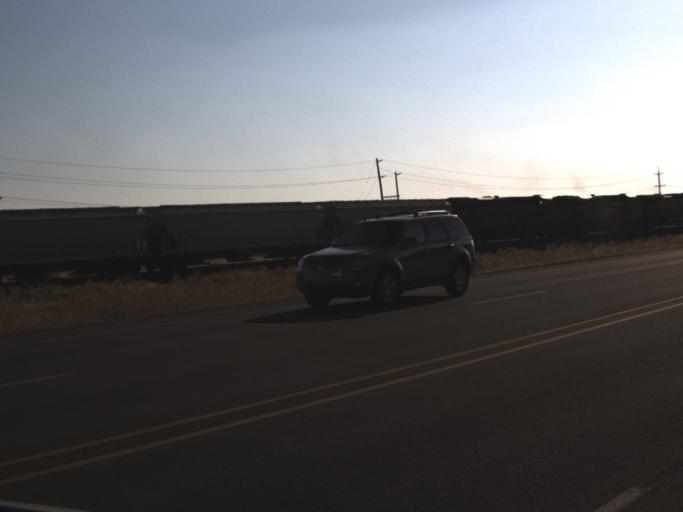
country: US
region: Washington
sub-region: Spokane County
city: Trentwood
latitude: 47.6970
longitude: -117.1705
